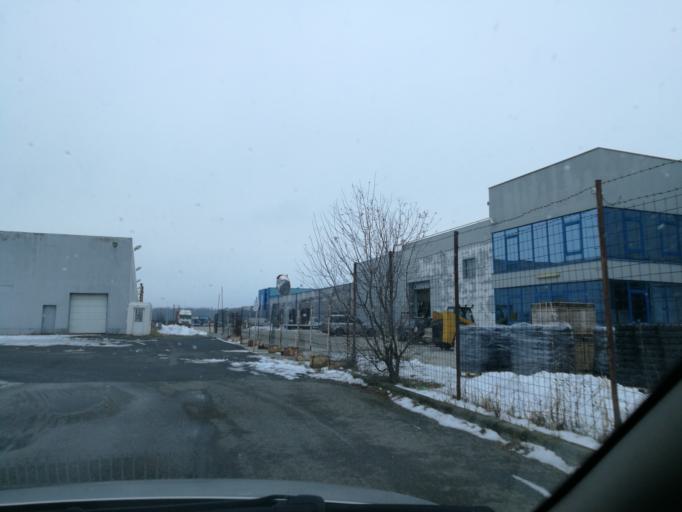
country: RO
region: Ilfov
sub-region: Comuna Tunari
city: Tunari
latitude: 44.5393
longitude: 26.1320
